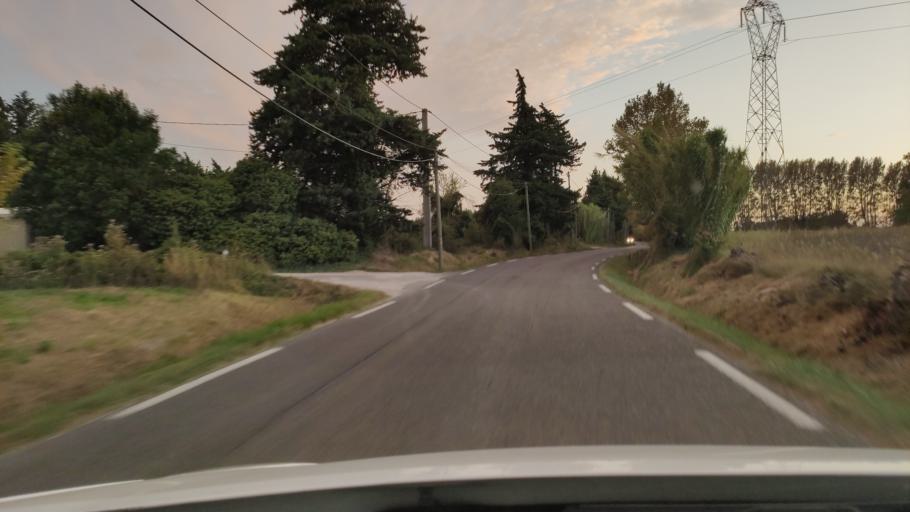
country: FR
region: Provence-Alpes-Cote d'Azur
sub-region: Departement du Vaucluse
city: Velleron
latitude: 43.9488
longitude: 5.0167
